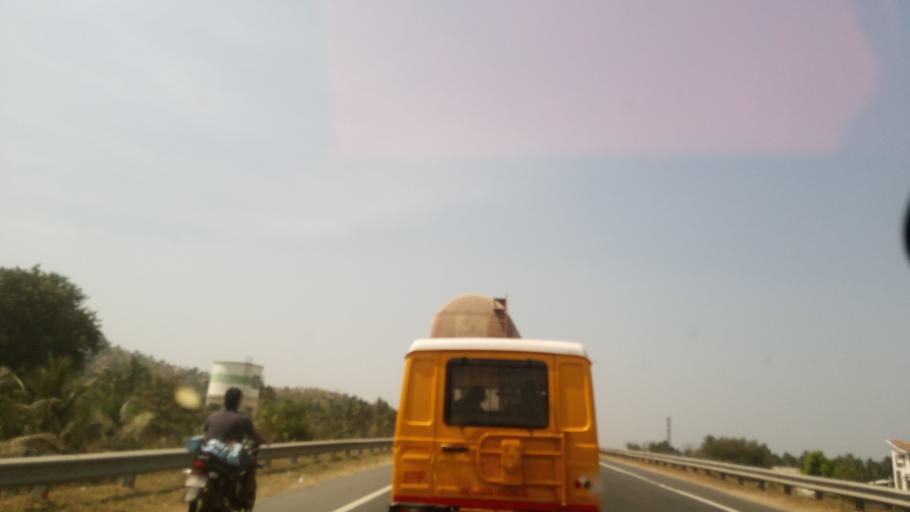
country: IN
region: Tamil Nadu
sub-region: Salem
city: Salem
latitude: 11.6602
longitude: 78.2166
